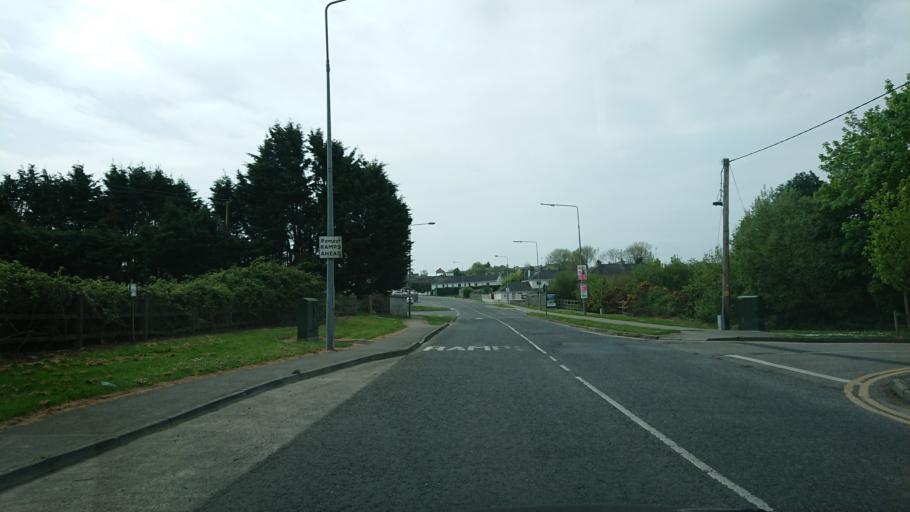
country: IE
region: Munster
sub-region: Waterford
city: Waterford
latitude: 52.2327
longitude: -7.0618
